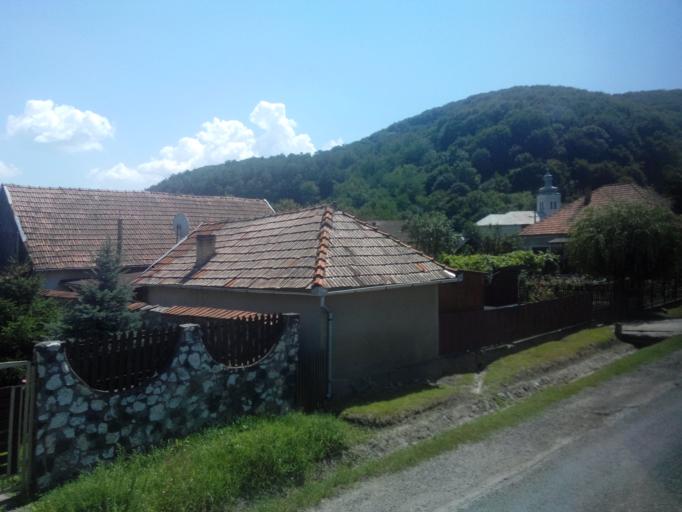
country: RO
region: Hunedoara
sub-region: Comuna Ilia
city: Ilia
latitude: 45.9221
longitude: 22.6721
